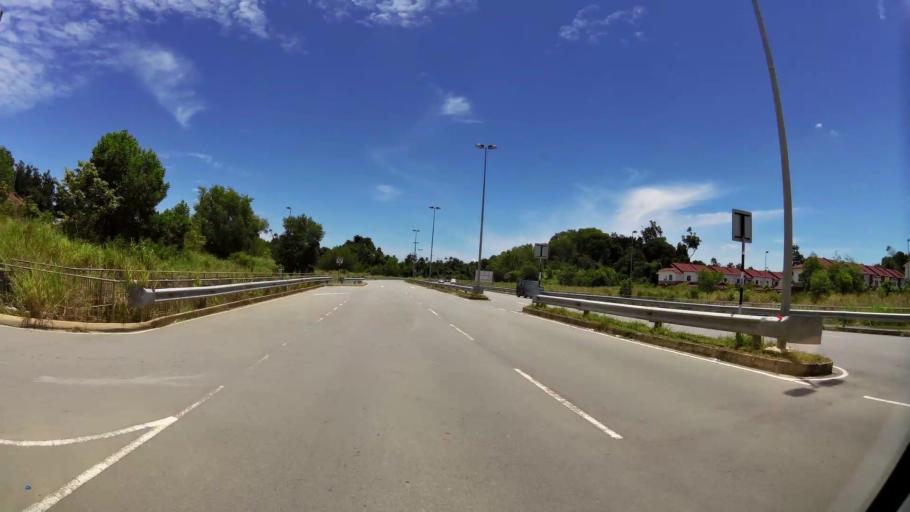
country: BN
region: Brunei and Muara
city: Bandar Seri Begawan
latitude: 5.0106
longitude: 115.0236
